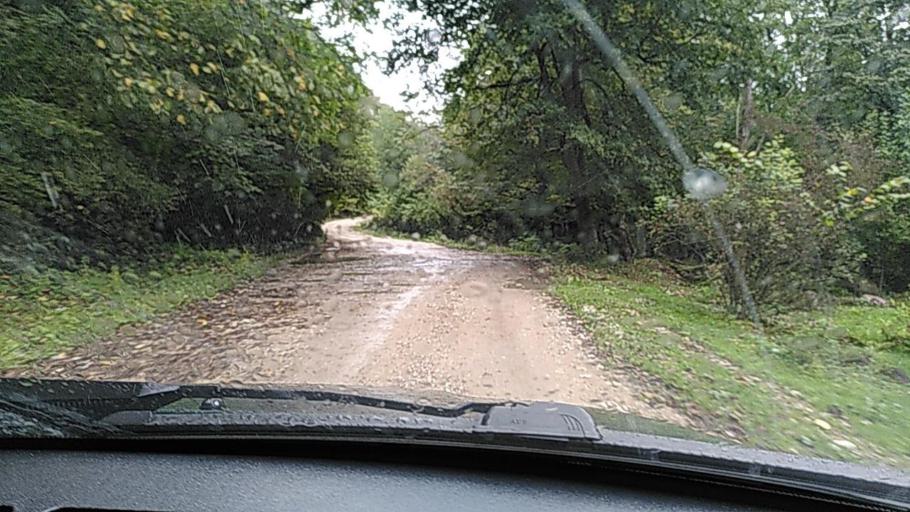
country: RU
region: Kabardino-Balkariya
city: Belaya Rechka
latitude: 43.4147
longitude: 43.4746
